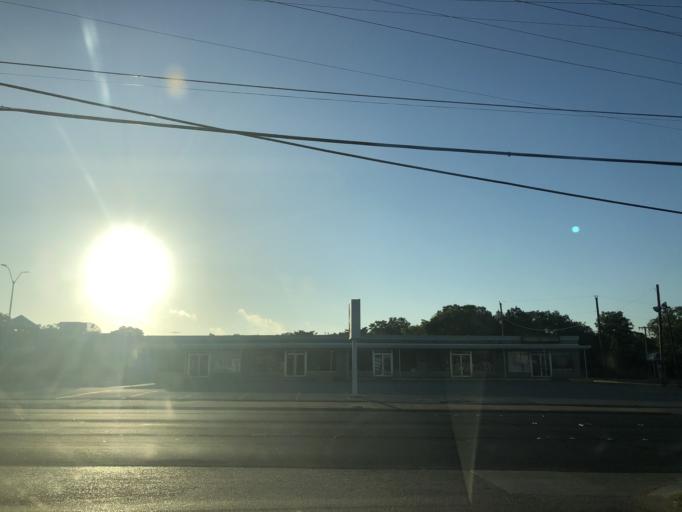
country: US
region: Texas
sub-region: Dallas County
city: Duncanville
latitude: 32.6395
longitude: -96.9087
